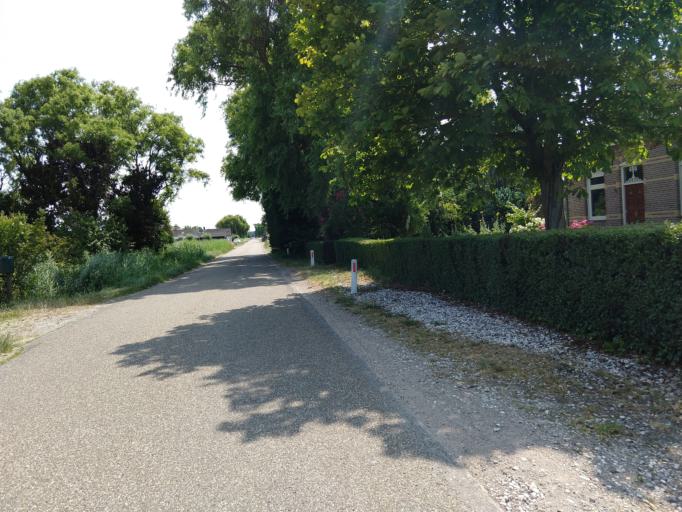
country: NL
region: Zeeland
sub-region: Gemeente Borsele
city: Borssele
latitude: 51.4588
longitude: 3.7757
